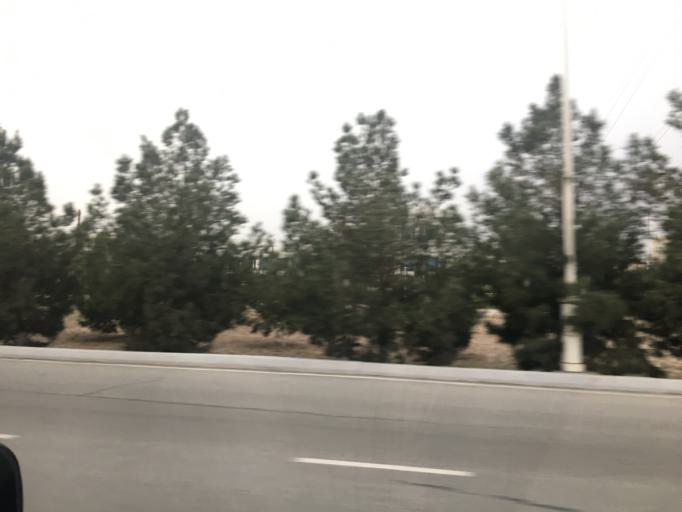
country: TM
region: Lebap
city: Turkmenabat
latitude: 39.0442
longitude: 63.5884
